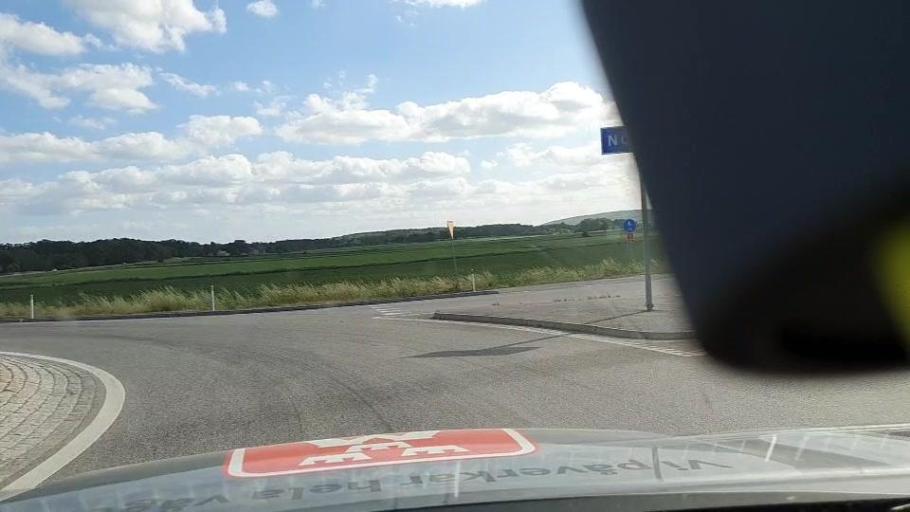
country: SE
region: Blekinge
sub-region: Karlshamns Kommun
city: Morrum
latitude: 56.1119
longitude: 14.6751
